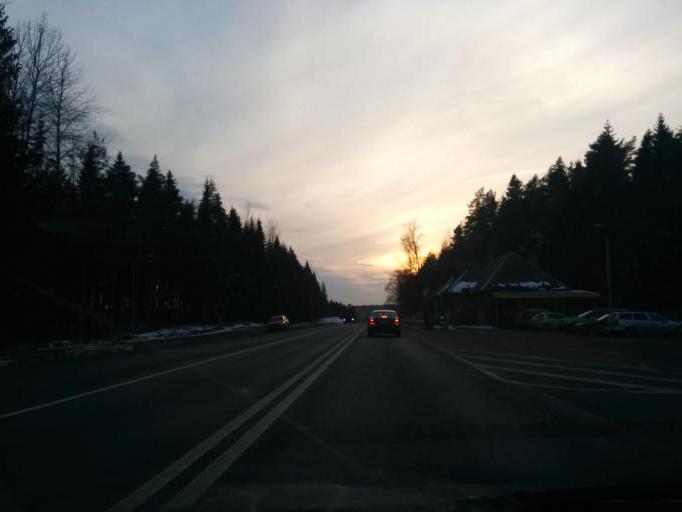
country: LV
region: Amatas Novads
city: Drabesi
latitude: 57.2263
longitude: 25.2505
